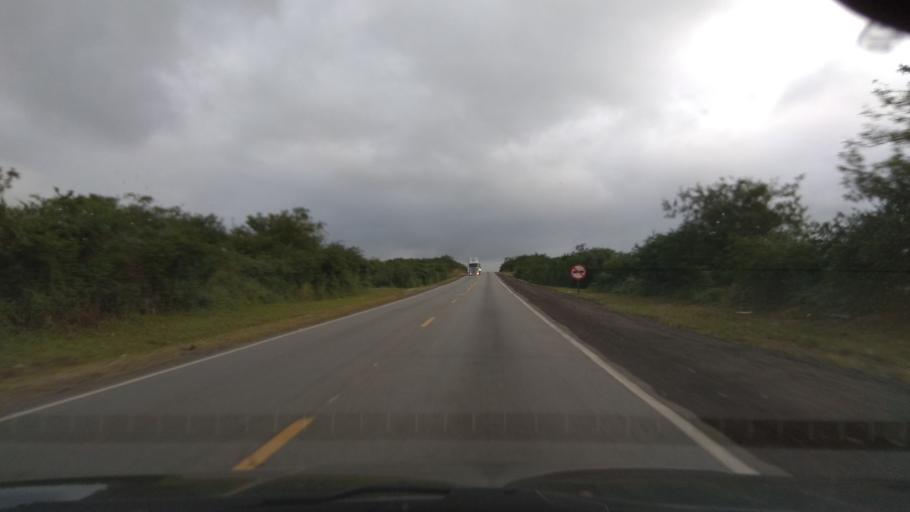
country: BR
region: Bahia
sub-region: Jaguaquara
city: Jaguaquara
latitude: -13.4189
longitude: -40.0266
